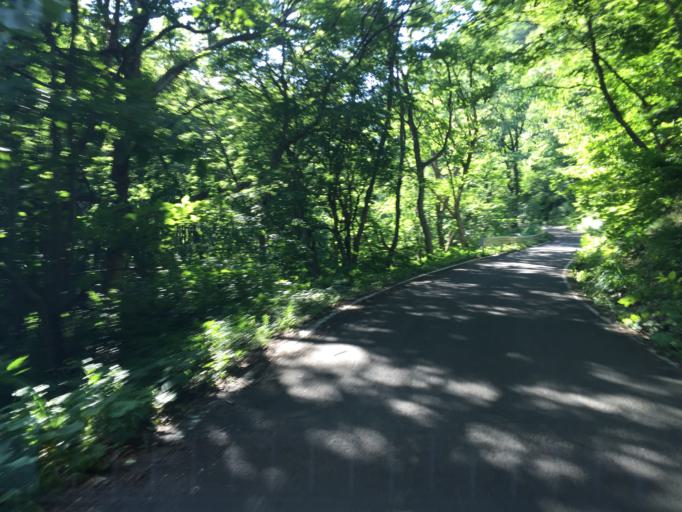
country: JP
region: Yamagata
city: Takahata
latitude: 37.9667
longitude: 140.3318
